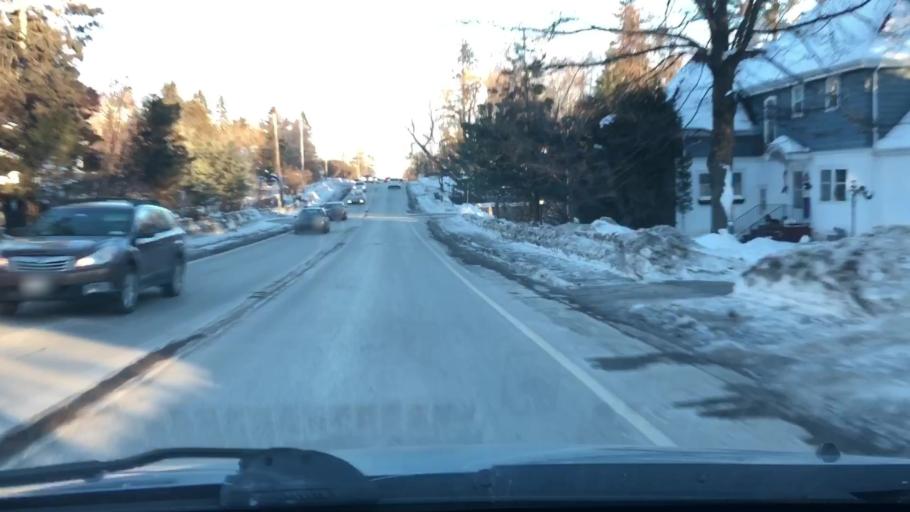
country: US
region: Minnesota
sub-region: Saint Louis County
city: Duluth
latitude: 46.8257
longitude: -92.0748
